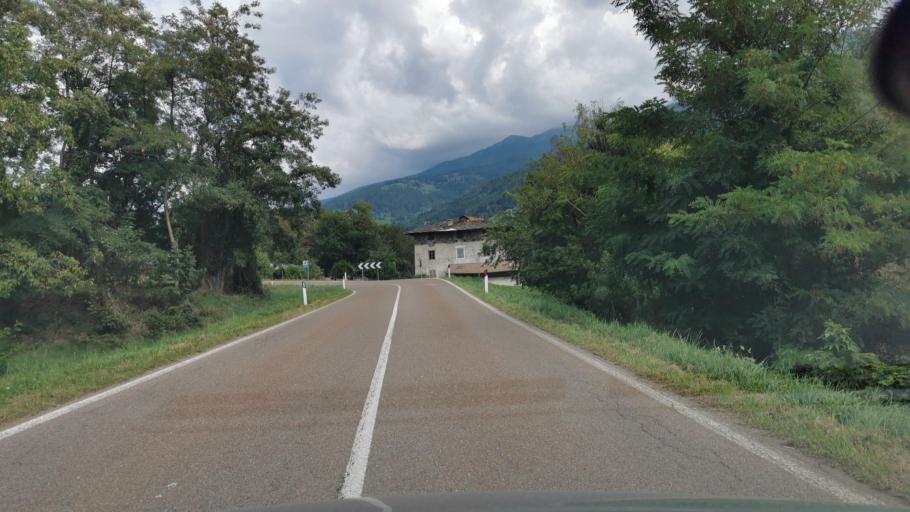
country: IT
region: Trentino-Alto Adige
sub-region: Provincia di Trento
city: Frassilongo
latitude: 46.0850
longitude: 11.2785
